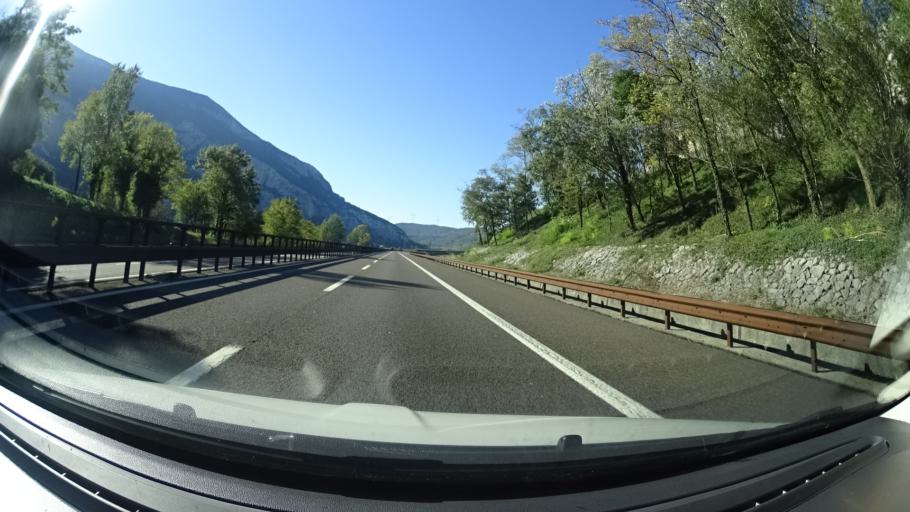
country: IT
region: Veneto
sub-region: Provincia di Verona
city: Dolce
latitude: 45.5924
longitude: 10.8379
